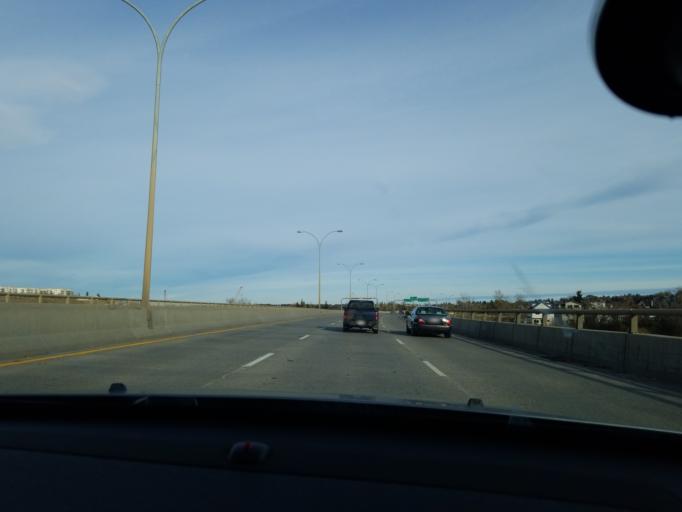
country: CA
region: Alberta
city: Edmonton
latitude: 53.5355
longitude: -113.4892
